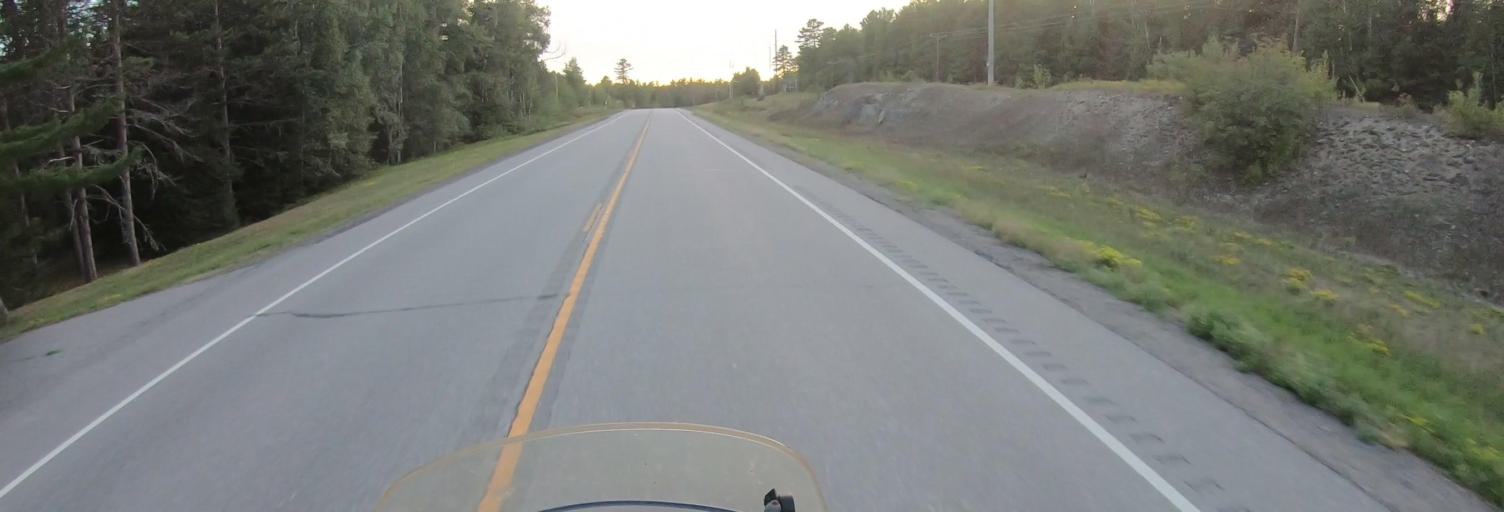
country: US
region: Minnesota
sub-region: Saint Louis County
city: Babbitt
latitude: 47.8538
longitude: -92.0541
